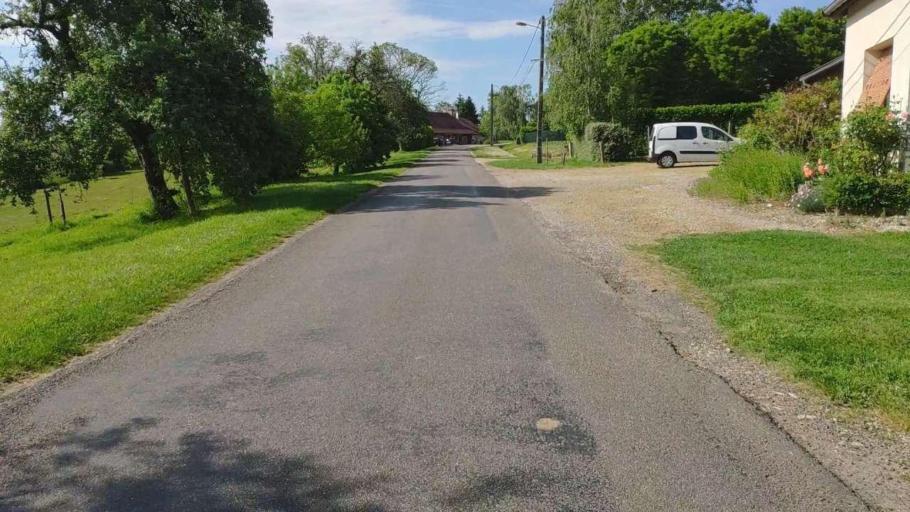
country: FR
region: Franche-Comte
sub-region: Departement du Jura
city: Bletterans
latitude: 46.7128
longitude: 5.4700
